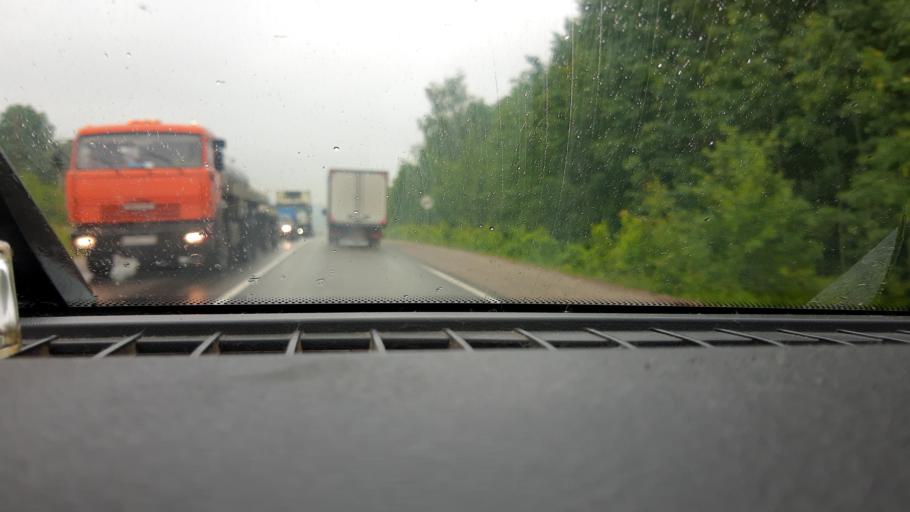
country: RU
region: Bashkortostan
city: Belebey
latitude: 54.2215
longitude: 54.0753
